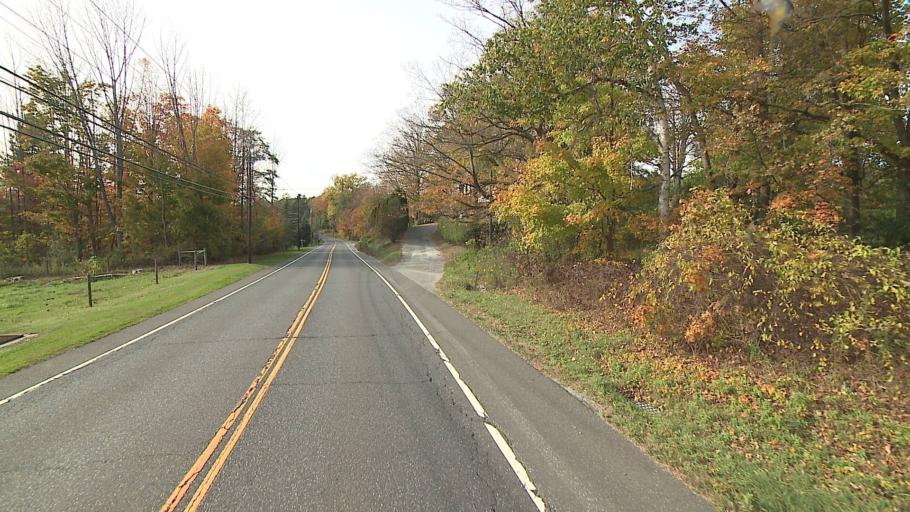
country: US
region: Connecticut
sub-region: Litchfield County
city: Canaan
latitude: 42.0171
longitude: -73.3021
